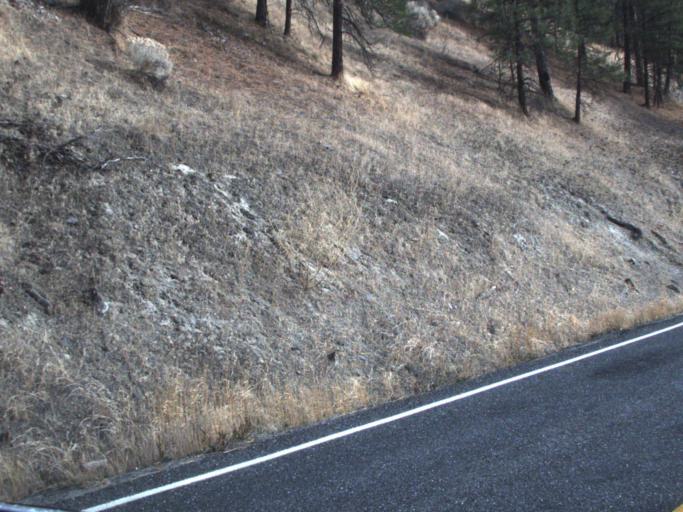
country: US
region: Washington
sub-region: Stevens County
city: Kettle Falls
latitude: 48.3337
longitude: -118.1557
